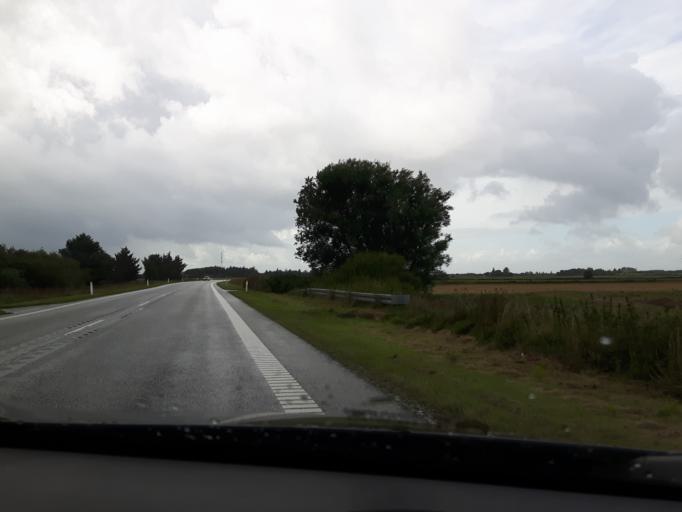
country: DK
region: North Denmark
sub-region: Jammerbugt Kommune
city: Fjerritslev
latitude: 57.0528
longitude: 9.1787
